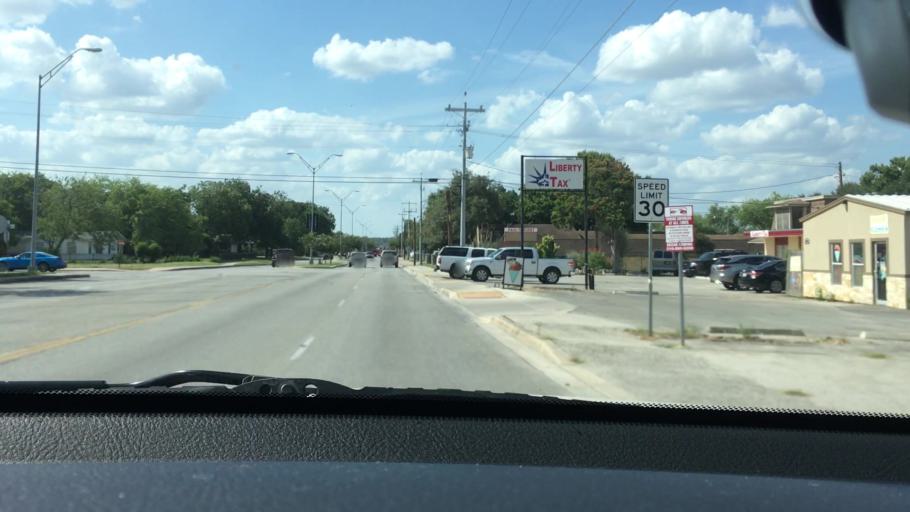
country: US
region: Texas
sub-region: Guadalupe County
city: Schertz
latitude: 29.5556
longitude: -98.2638
